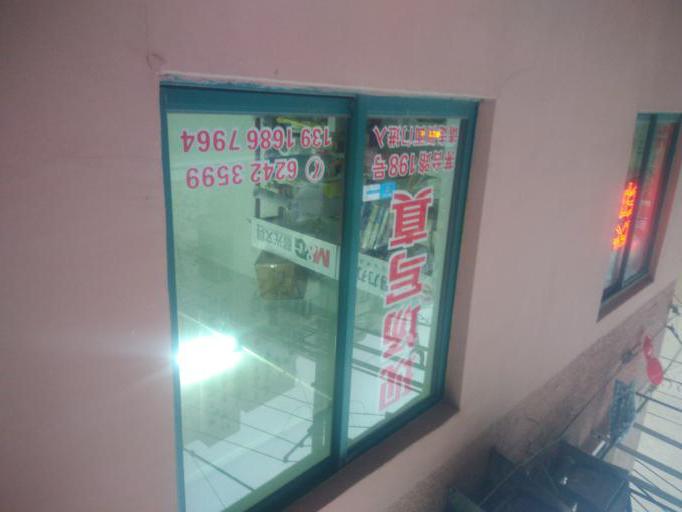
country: CN
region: Shanghai Shi
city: Changning
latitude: 31.2117
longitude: 121.3972
